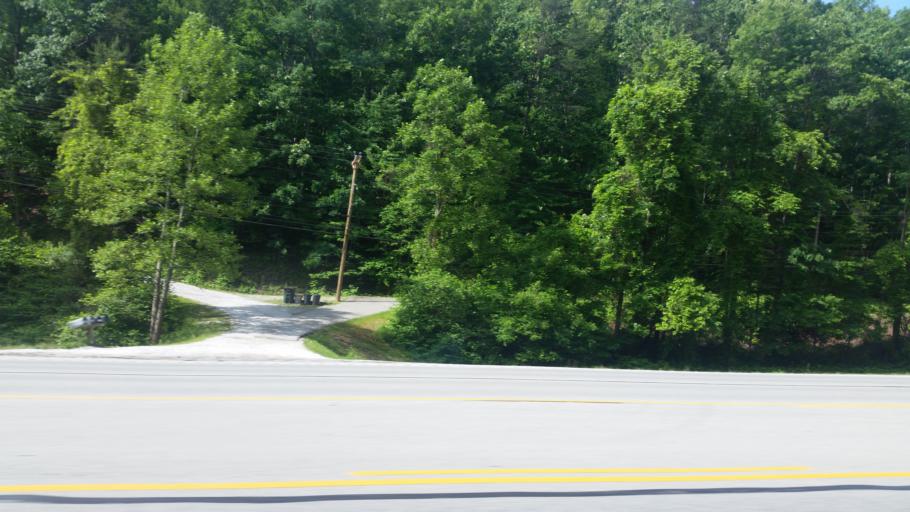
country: US
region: Kentucky
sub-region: Rowan County
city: Morehead
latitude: 38.1800
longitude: -83.4642
